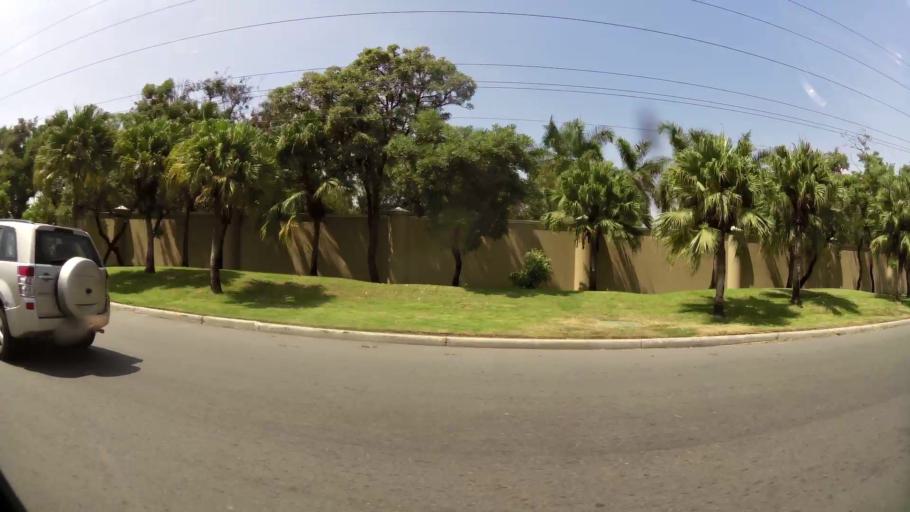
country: EC
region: Guayas
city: Eloy Alfaro
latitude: -2.0943
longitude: -79.8737
